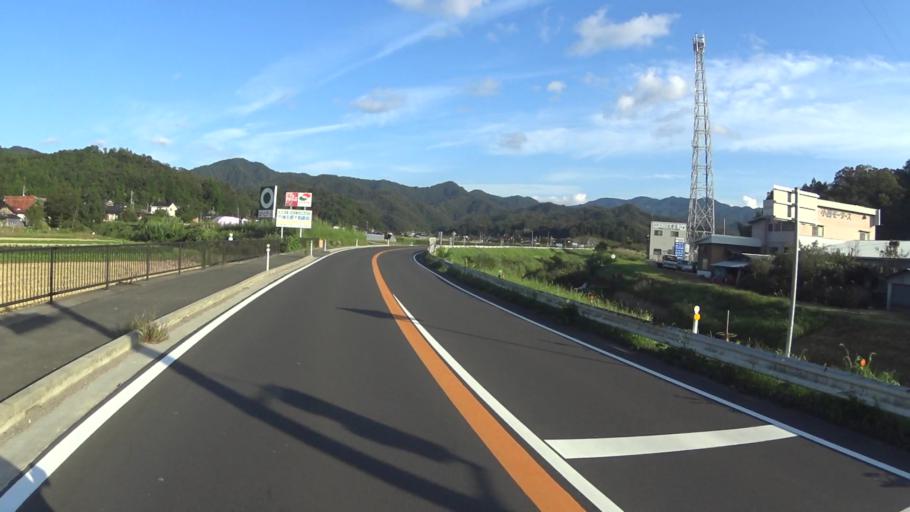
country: JP
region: Hyogo
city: Toyooka
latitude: 35.5788
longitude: 134.9725
